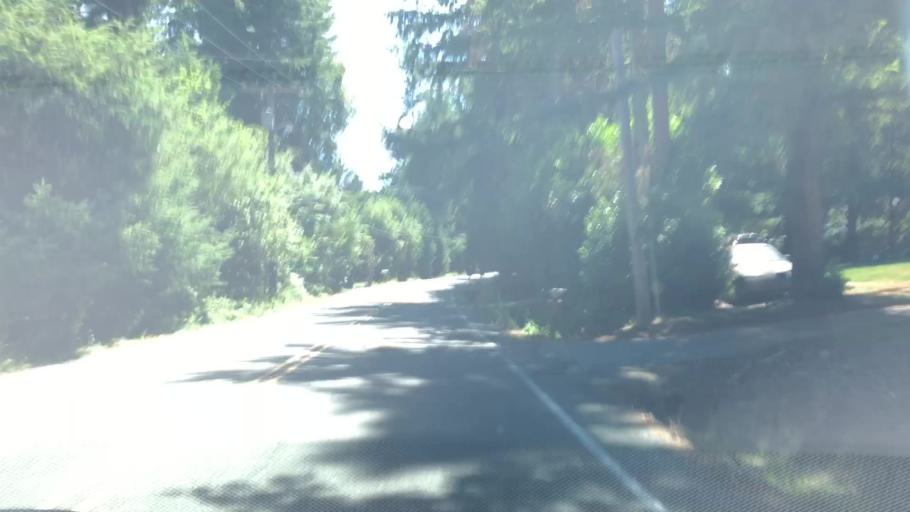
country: US
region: Washington
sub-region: King County
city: Cottage Lake
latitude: 47.7513
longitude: -122.1074
